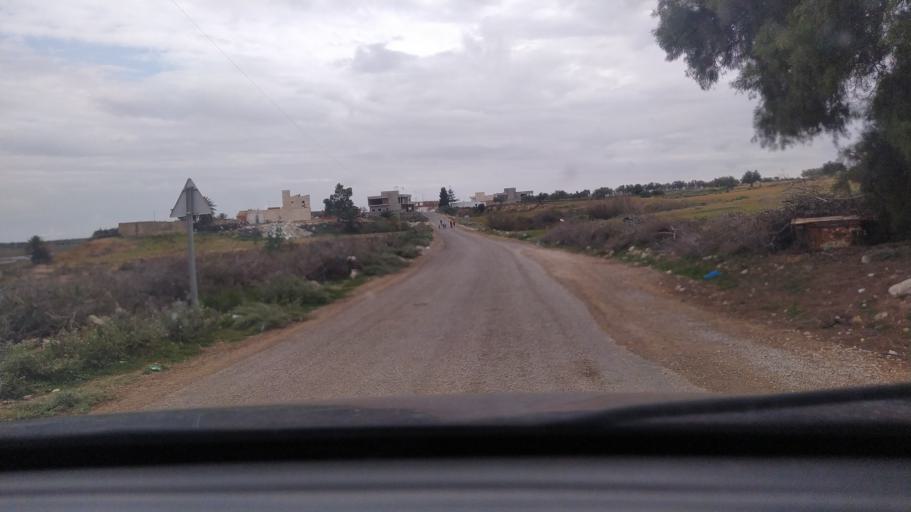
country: TN
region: Al Munastir
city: Sidi Bin Nur
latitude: 35.5173
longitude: 10.9662
